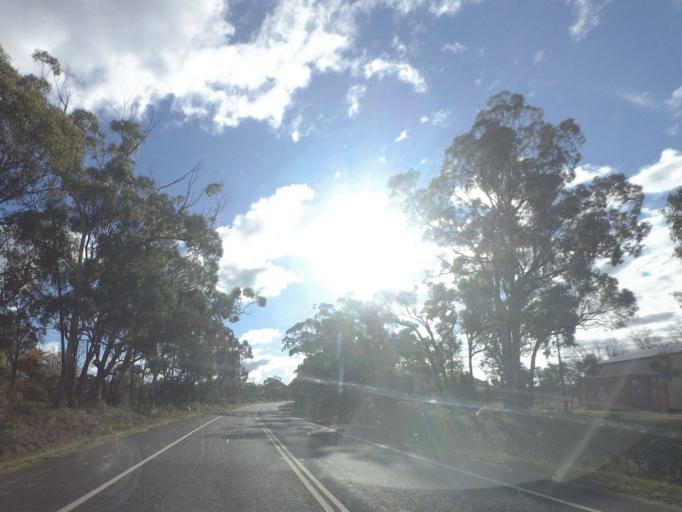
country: AU
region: Victoria
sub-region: Mount Alexander
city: Castlemaine
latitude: -37.0981
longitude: 144.3293
